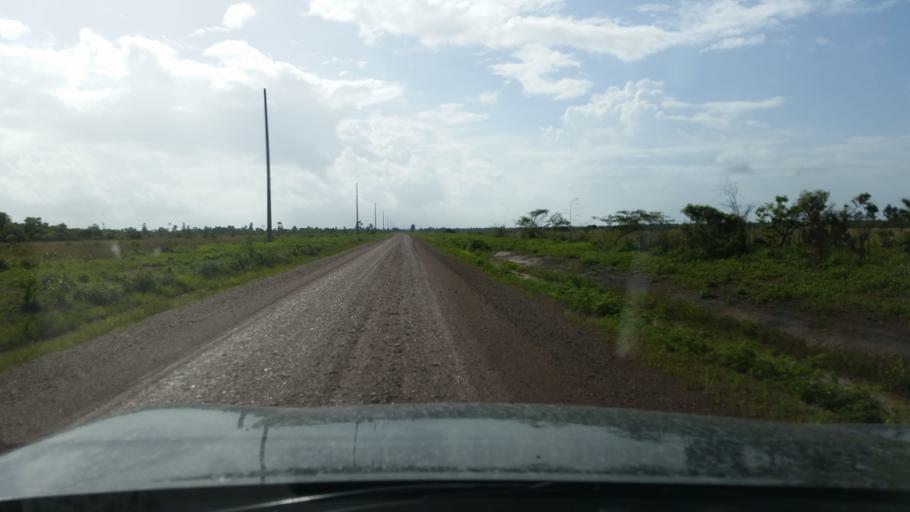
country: NI
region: Atlantico Norte (RAAN)
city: Puerto Cabezas
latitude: 14.1090
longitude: -83.5827
